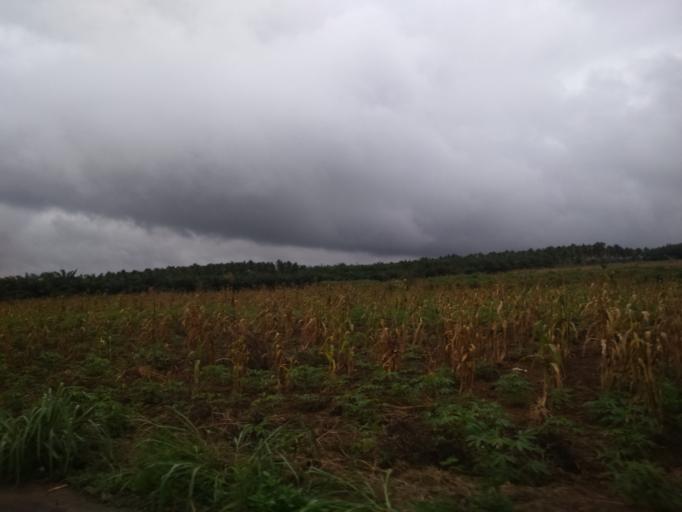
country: CI
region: Sud-Comoe
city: Adiake
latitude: 5.3008
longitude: -3.3527
